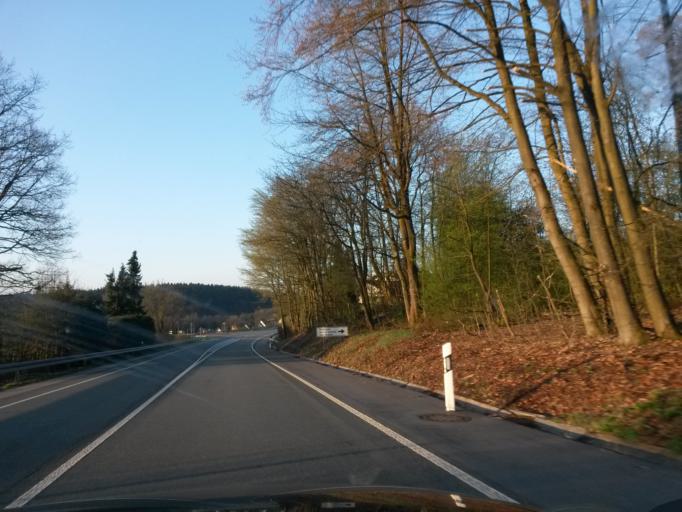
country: DE
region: North Rhine-Westphalia
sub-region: Regierungsbezirk Arnsberg
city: Herscheid
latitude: 51.1233
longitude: 7.7487
